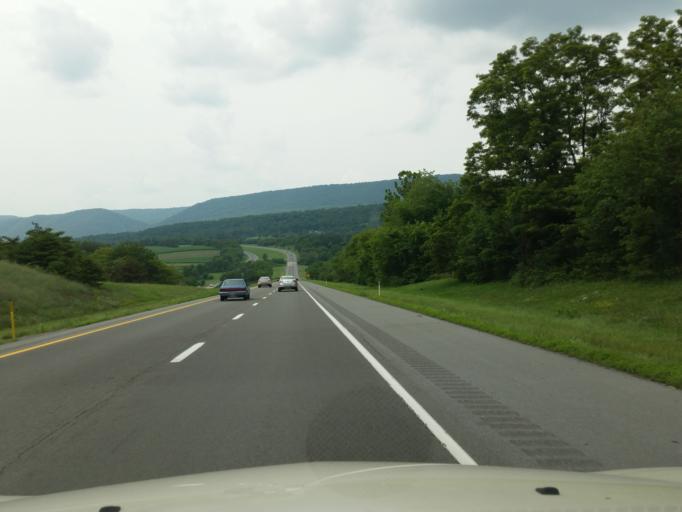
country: US
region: Pennsylvania
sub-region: Juniata County
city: Mifflintown
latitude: 40.5985
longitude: -77.3847
